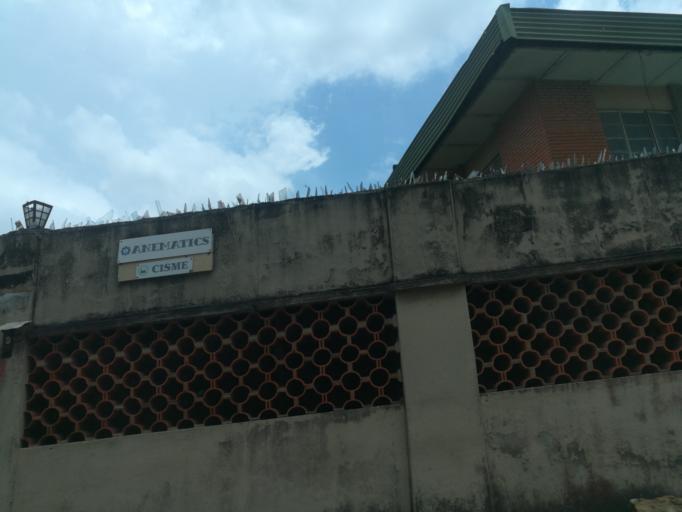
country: NG
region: Lagos
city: Somolu
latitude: 6.5520
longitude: 3.3604
